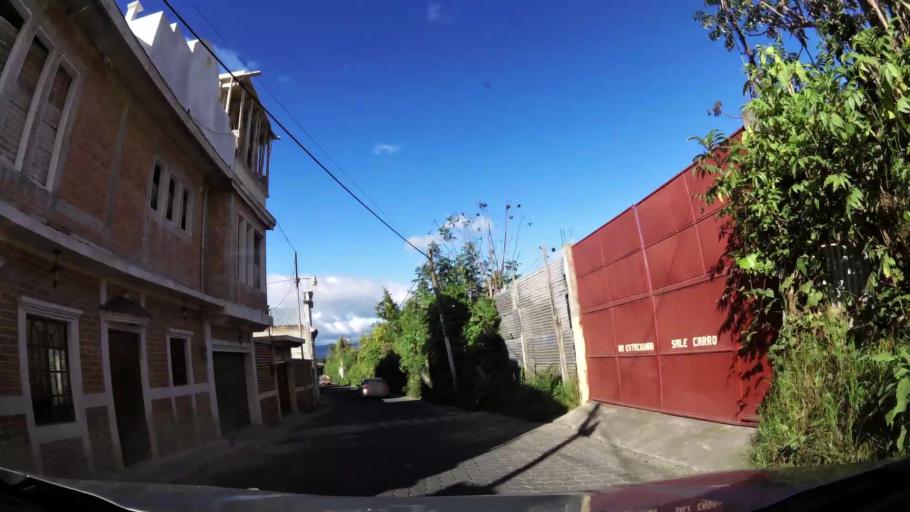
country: GT
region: Quiche
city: Chichicastenango
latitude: 14.9461
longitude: -91.1081
